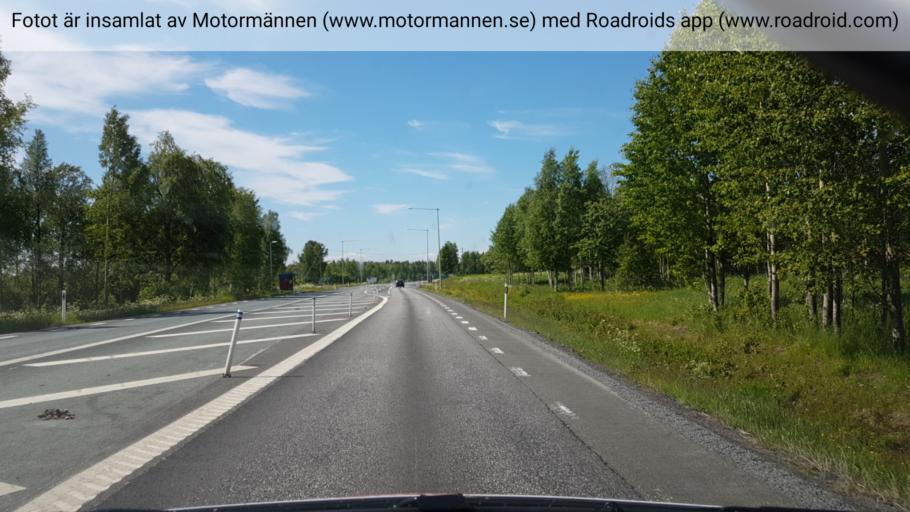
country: SE
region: Norrbotten
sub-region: Haparanda Kommun
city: Haparanda
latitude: 65.8090
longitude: 23.9829
